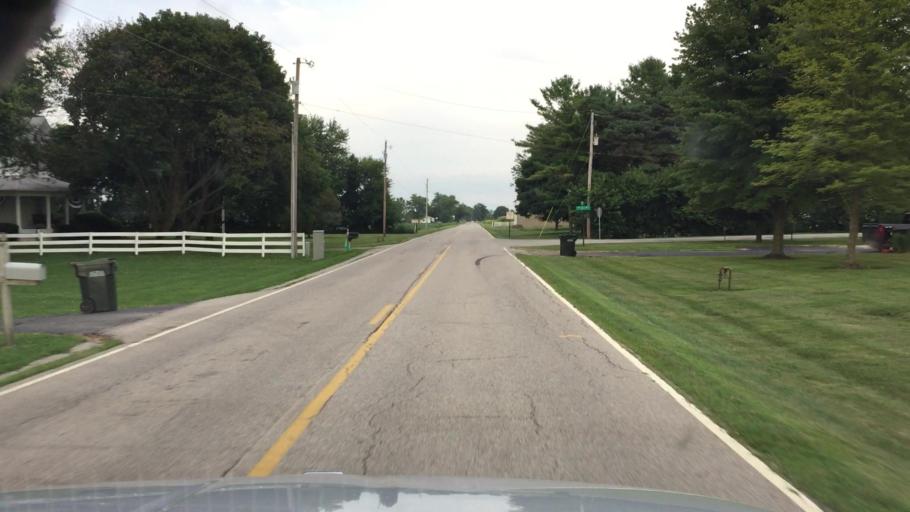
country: US
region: Ohio
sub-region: Madison County
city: Plain City
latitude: 40.0746
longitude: -83.2308
